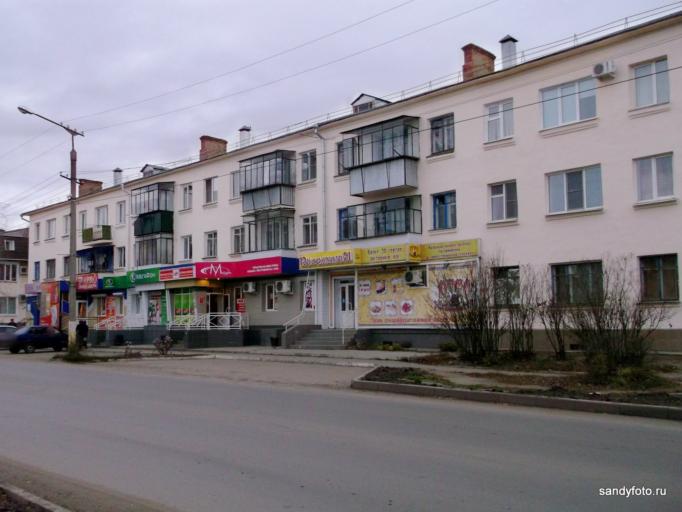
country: RU
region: Chelyabinsk
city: Troitsk
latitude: 54.0828
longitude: 61.5397
